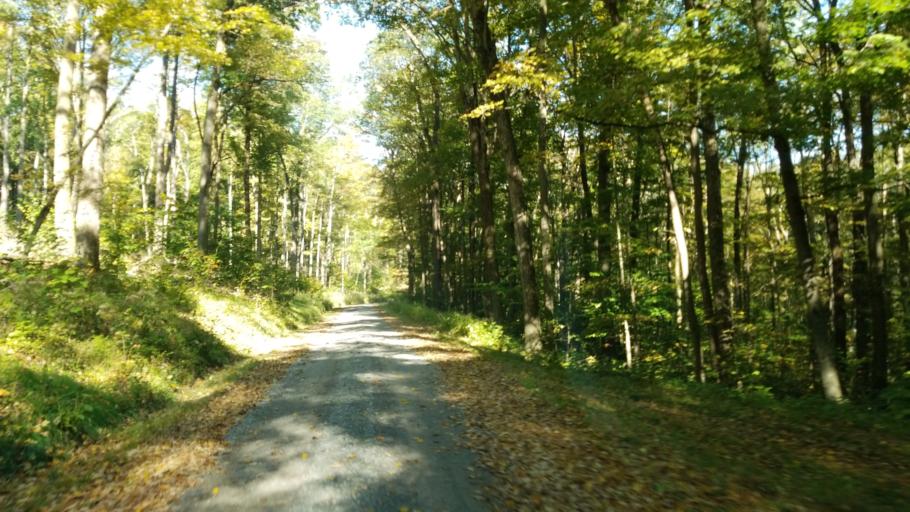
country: US
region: Pennsylvania
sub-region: Clearfield County
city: Treasure Lake
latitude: 41.1414
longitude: -78.5737
